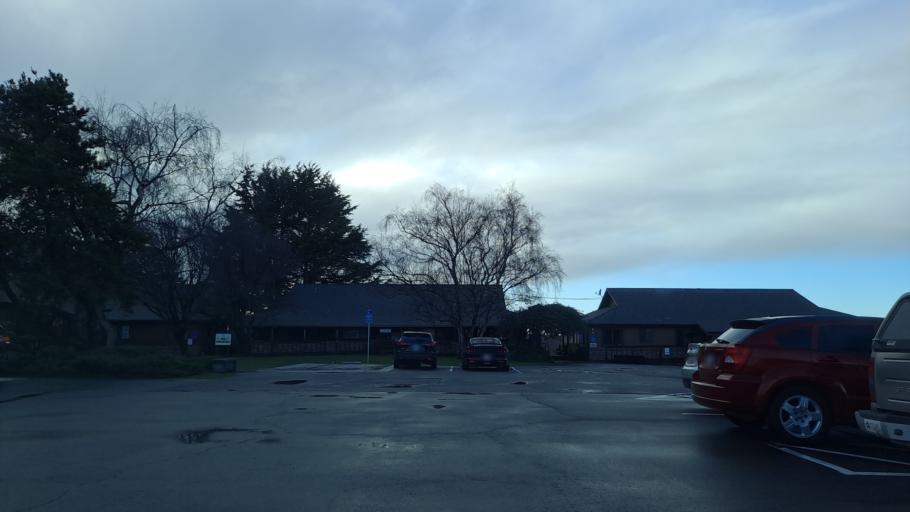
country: US
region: California
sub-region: Humboldt County
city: Fortuna
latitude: 40.5817
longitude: -124.1369
